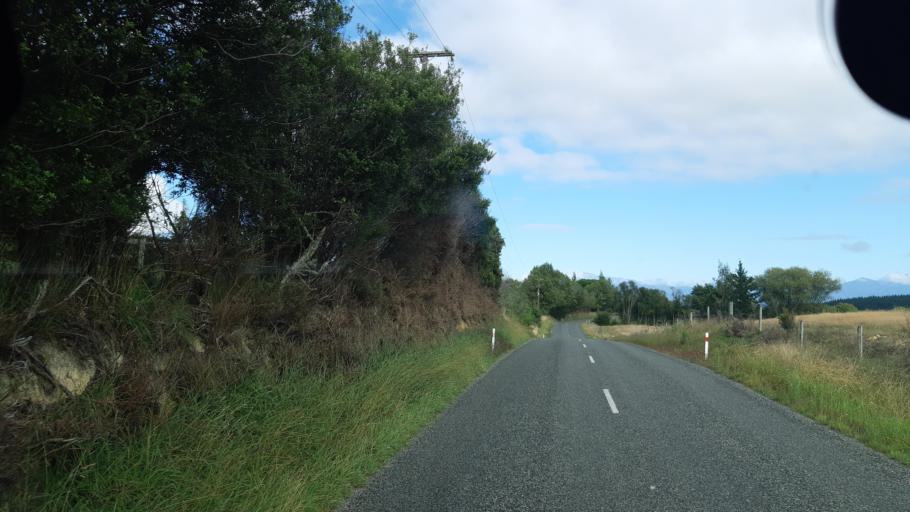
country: NZ
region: Tasman
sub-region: Tasman District
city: Mapua
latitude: -41.2440
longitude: 173.0489
